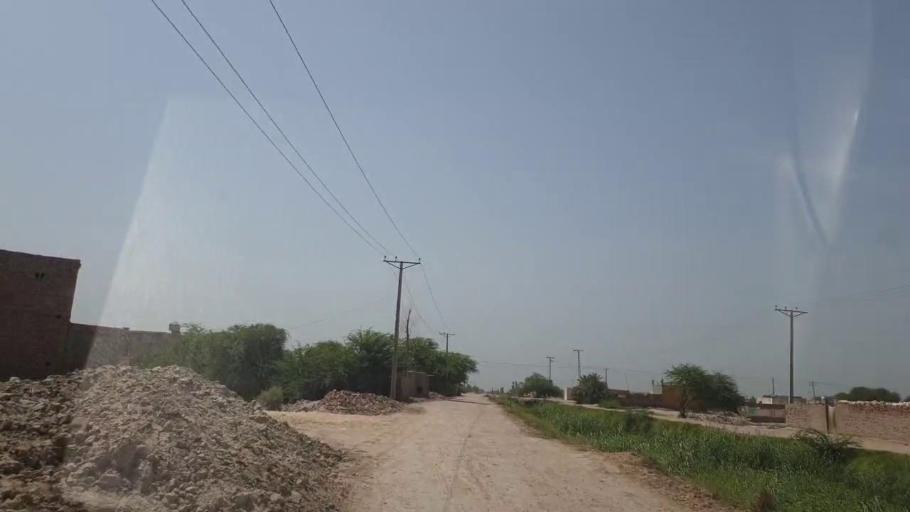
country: PK
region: Sindh
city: Ranipur
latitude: 27.2961
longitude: 68.5455
